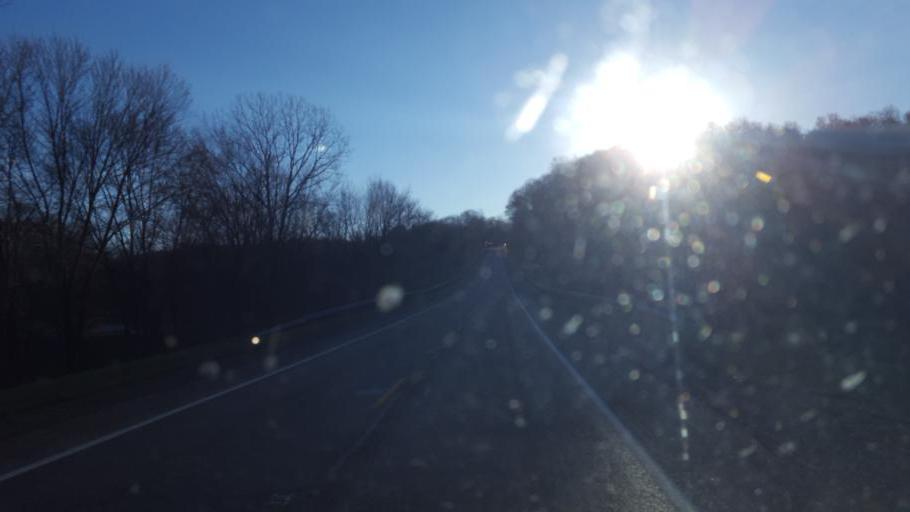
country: US
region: Ohio
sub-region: Ashland County
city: Loudonville
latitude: 40.6202
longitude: -82.1870
